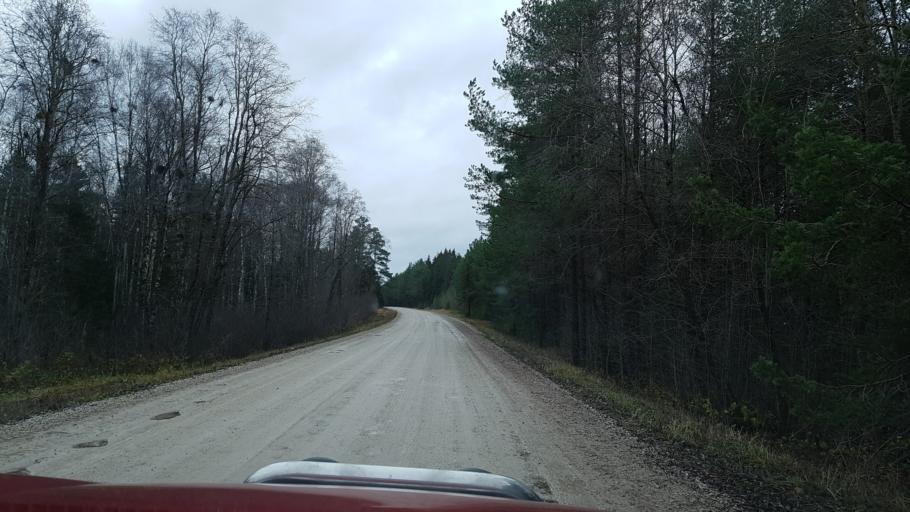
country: EE
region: Paernumaa
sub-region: Halinga vald
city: Parnu-Jaagupi
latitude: 58.5530
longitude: 24.4120
